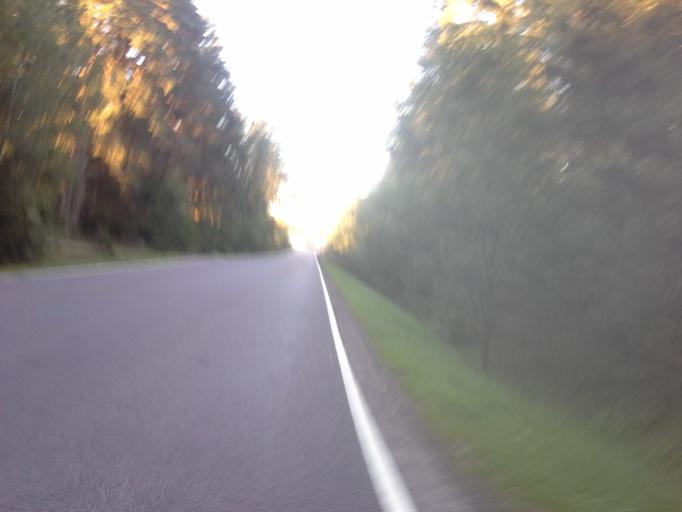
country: RU
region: Moskovskaya
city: Selyatino
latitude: 55.5138
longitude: 36.9397
